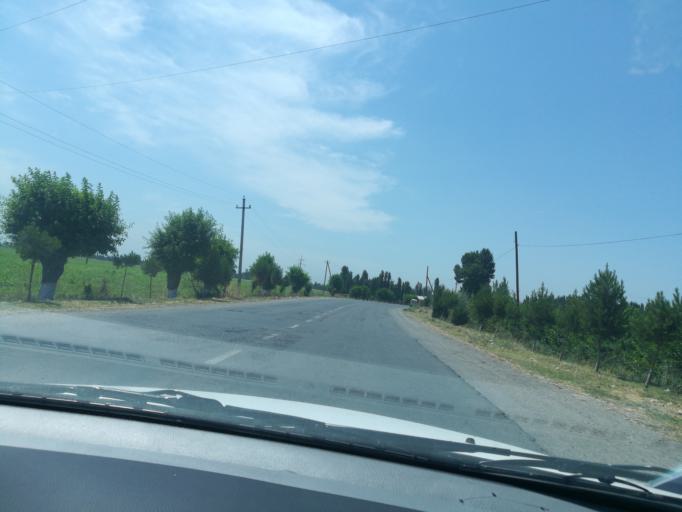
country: UZ
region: Namangan
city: Uchqurghon Shahri
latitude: 41.0902
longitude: 72.0592
